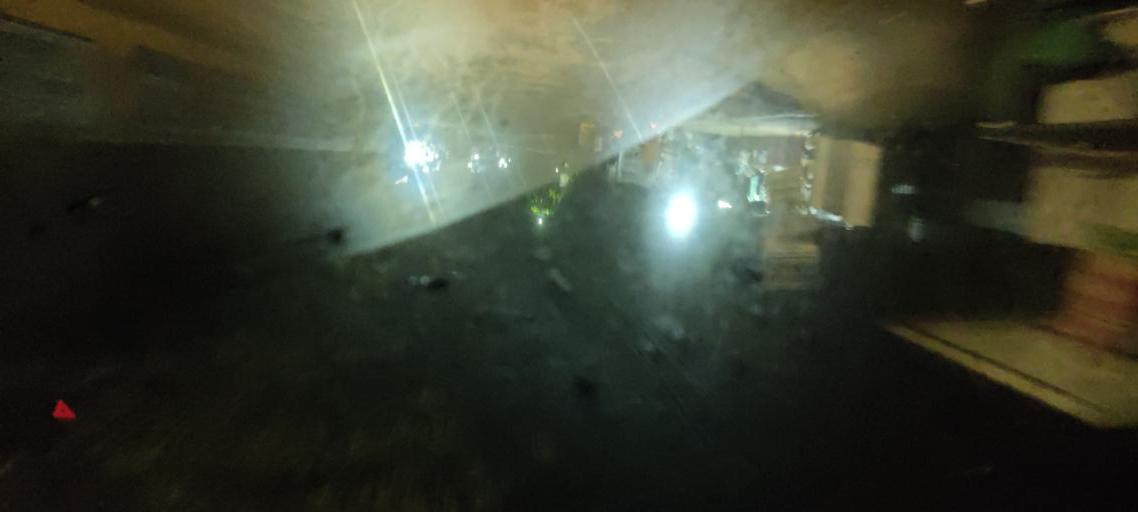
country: IN
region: Kerala
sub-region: Alappuzha
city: Vayalar
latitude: 9.7219
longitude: 76.3375
